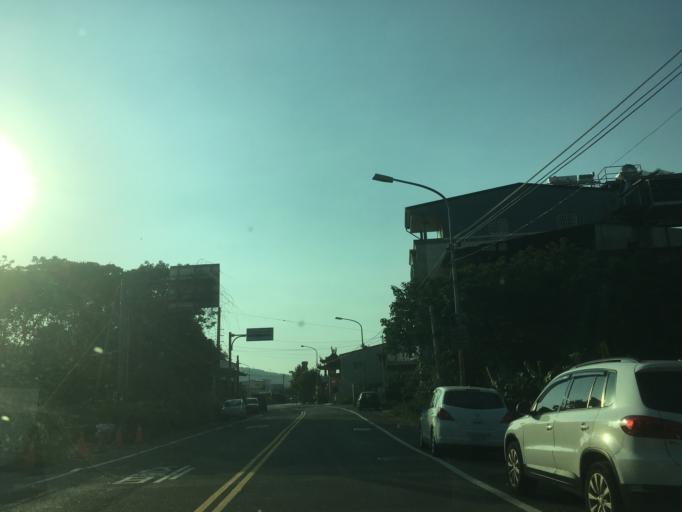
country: TW
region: Taiwan
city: Zhongxing New Village
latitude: 23.9526
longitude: 120.6623
